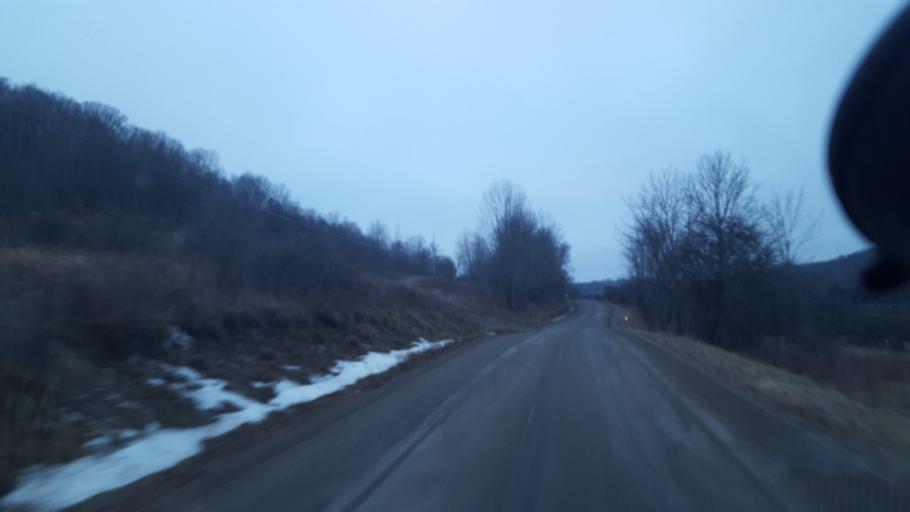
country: US
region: Pennsylvania
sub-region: Tioga County
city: Westfield
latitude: 41.9509
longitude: -77.6902
